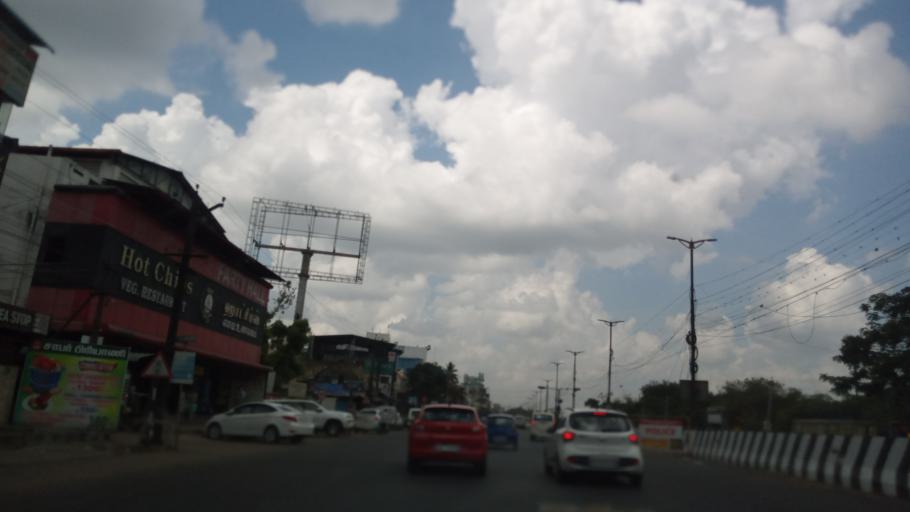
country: IN
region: Tamil Nadu
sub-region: Kancheepuram
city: Pallavaram
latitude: 12.9431
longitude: 80.1338
